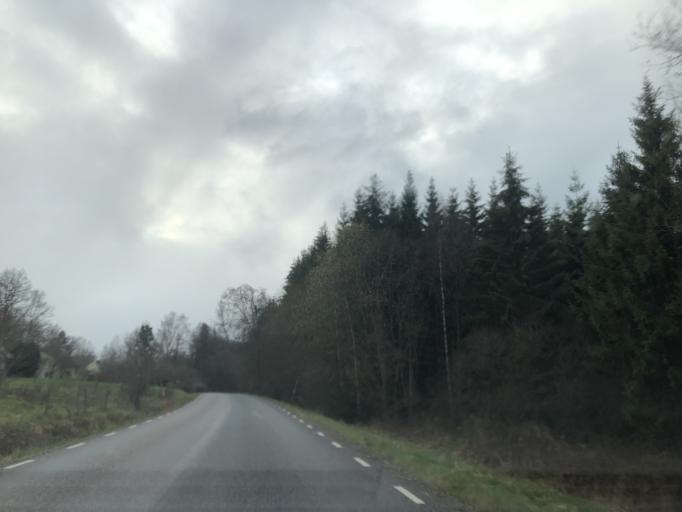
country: SE
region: Vaestra Goetaland
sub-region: Ulricehamns Kommun
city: Ulricehamn
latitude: 57.6765
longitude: 13.4072
